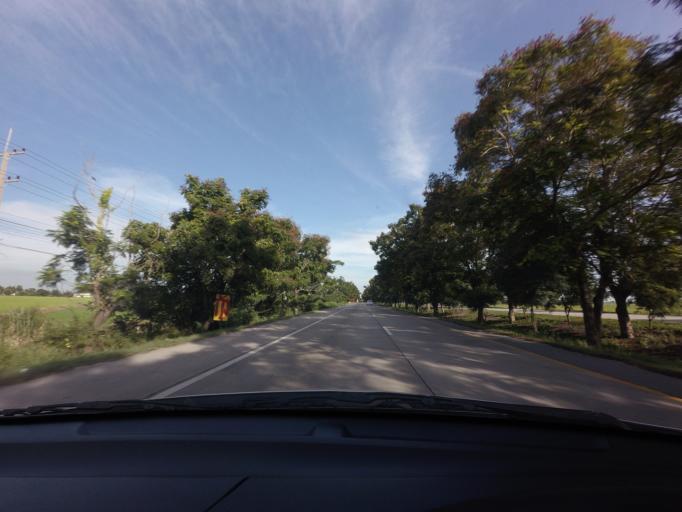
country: TH
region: Phra Nakhon Si Ayutthaya
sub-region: Amphoe Bang Sai
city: Bang Sai
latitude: 14.2908
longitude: 100.2384
